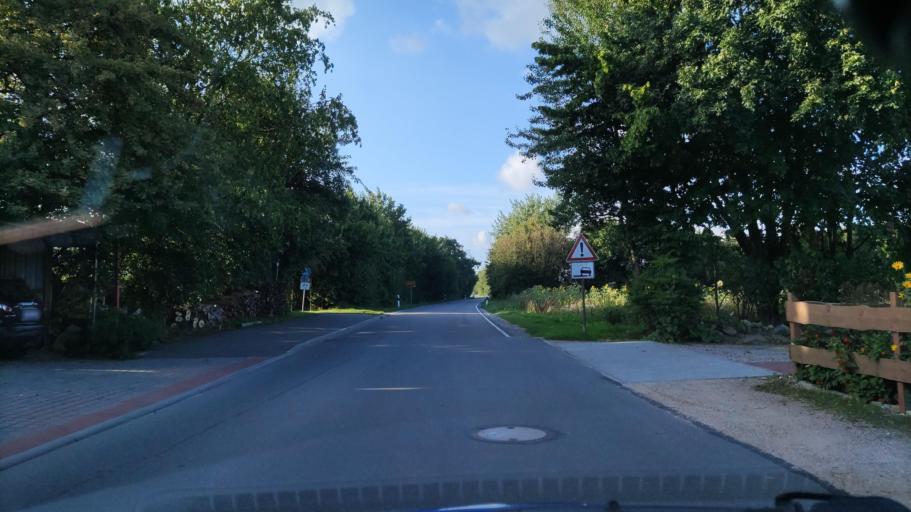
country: DE
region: Schleswig-Holstein
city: Glasau
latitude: 54.0799
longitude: 10.4990
